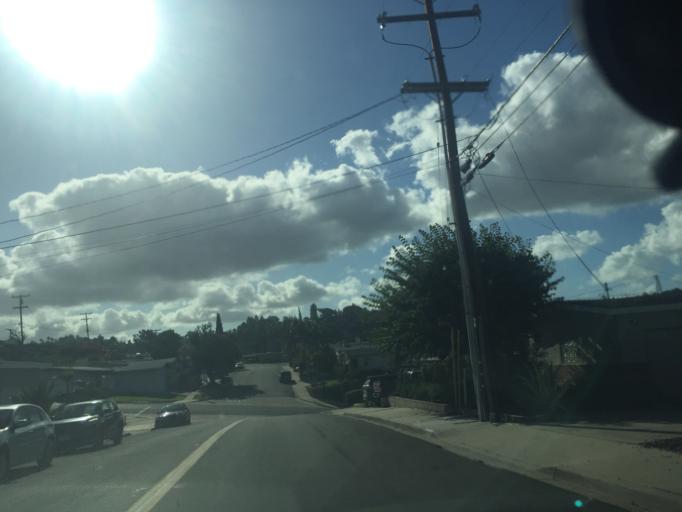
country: US
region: California
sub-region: San Diego County
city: La Mesa
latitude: 32.7856
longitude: -117.0940
